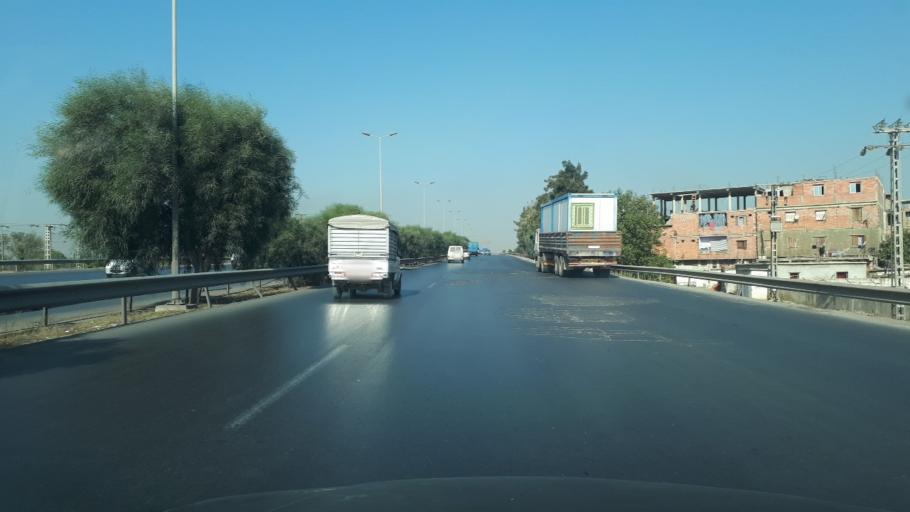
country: DZ
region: Tipaza
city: Baraki
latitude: 36.6822
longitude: 3.1045
